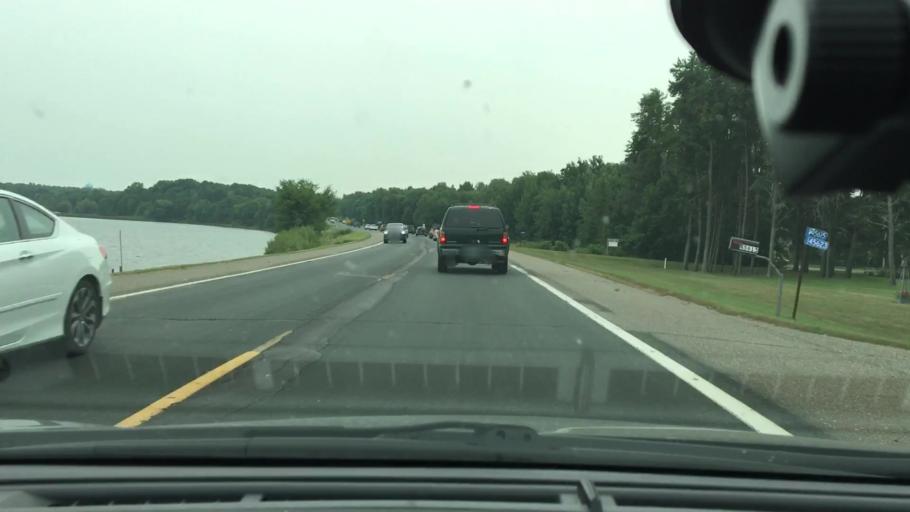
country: US
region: Minnesota
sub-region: Mille Lacs County
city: Vineland
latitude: 46.2093
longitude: -93.7897
